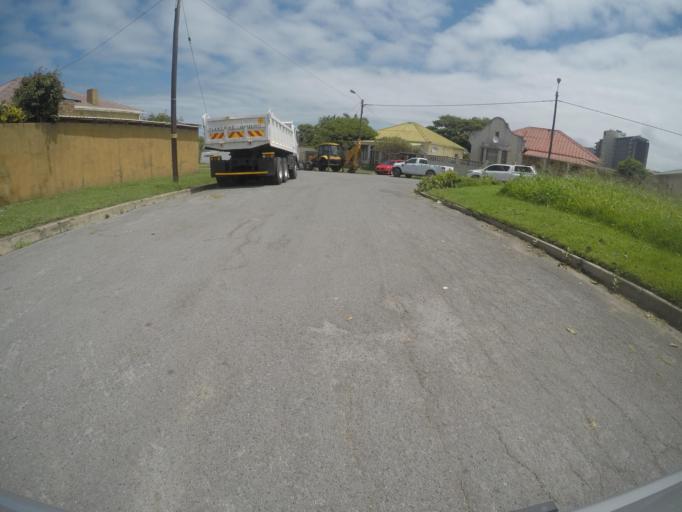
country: ZA
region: Eastern Cape
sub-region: Buffalo City Metropolitan Municipality
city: East London
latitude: -33.0215
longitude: 27.9100
